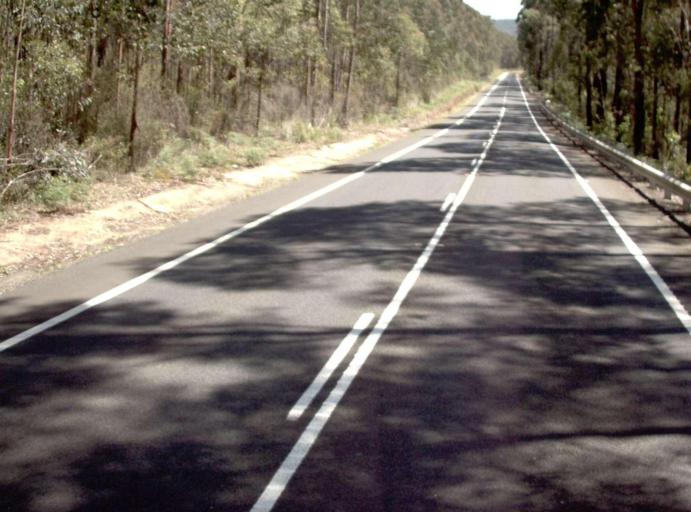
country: AU
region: New South Wales
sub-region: Bombala
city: Bombala
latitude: -37.5706
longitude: 149.0277
